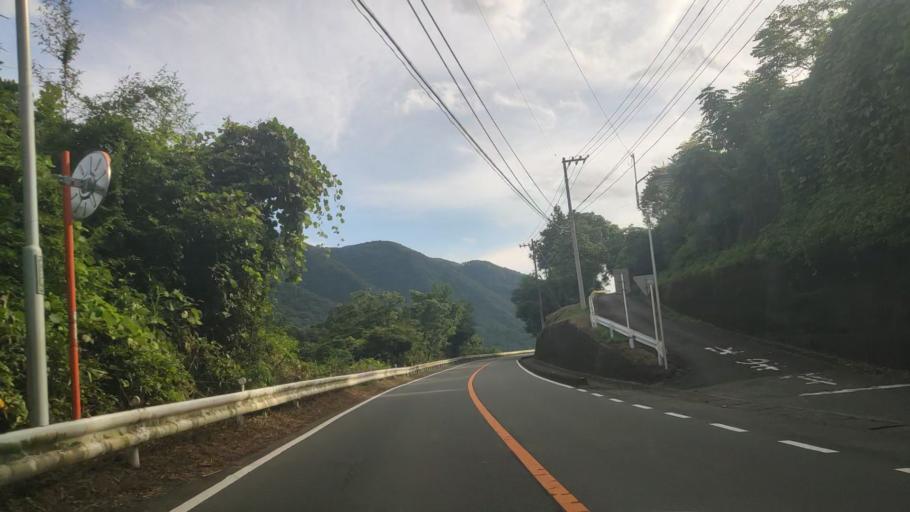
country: JP
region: Gunma
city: Omamacho-omama
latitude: 36.5327
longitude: 139.3324
